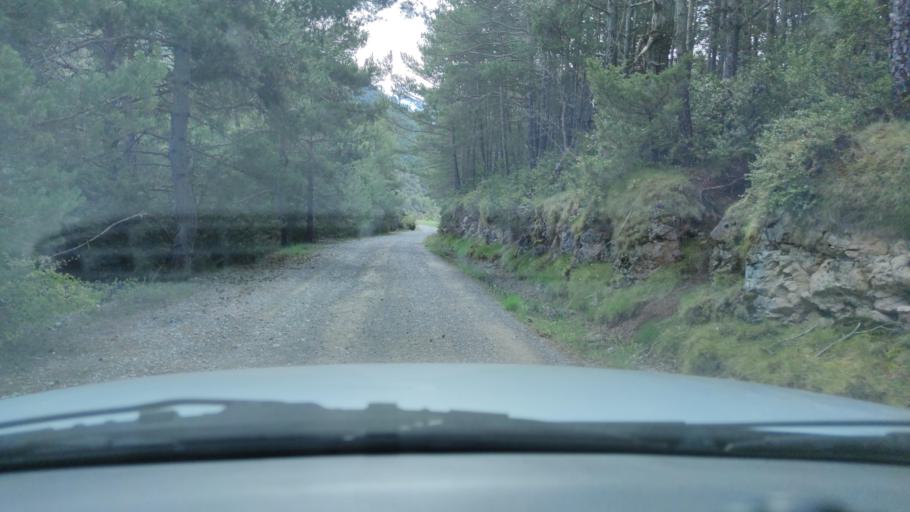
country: ES
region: Catalonia
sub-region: Provincia de Lleida
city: Coll de Nargo
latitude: 42.2523
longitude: 1.4059
